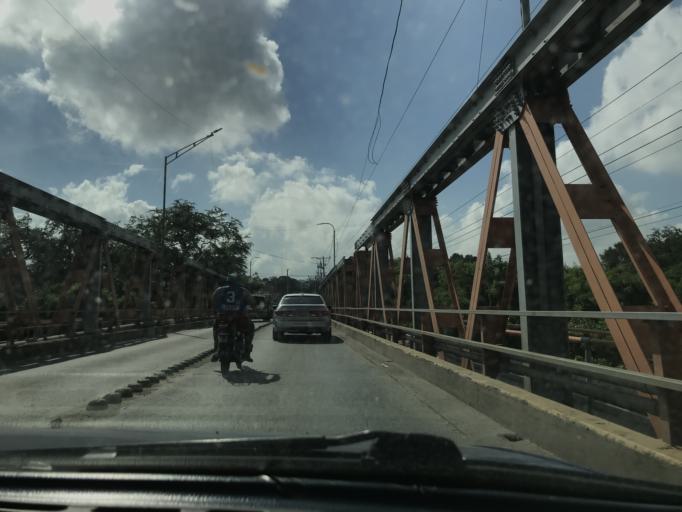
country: DO
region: Santiago
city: Santiago de los Caballeros
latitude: 19.4544
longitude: -70.7163
